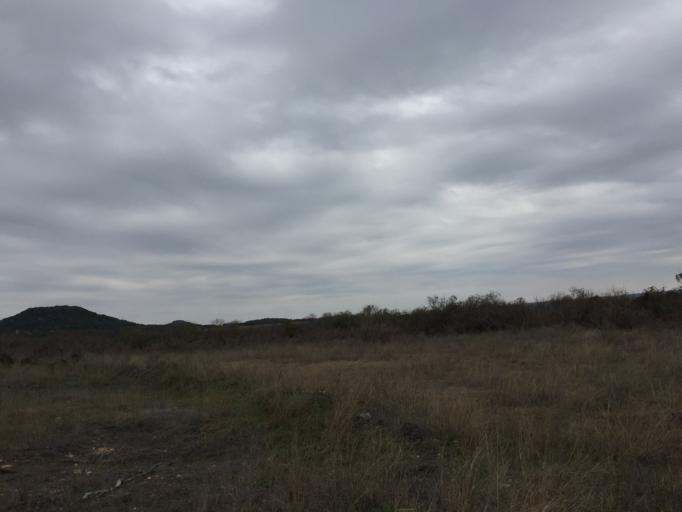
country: US
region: Texas
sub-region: Bell County
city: Nolanville
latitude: 31.0265
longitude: -97.6174
